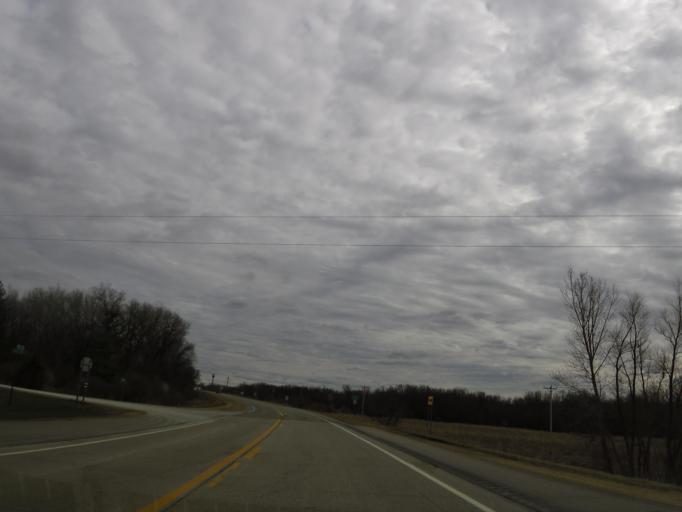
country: US
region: Minnesota
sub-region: Fillmore County
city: Spring Valley
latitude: 43.5009
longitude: -92.3691
